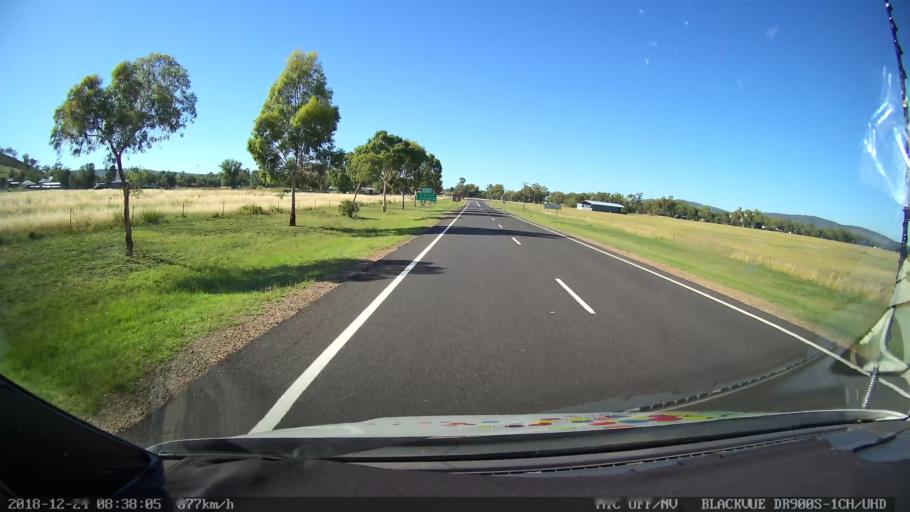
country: AU
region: New South Wales
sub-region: Liverpool Plains
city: Quirindi
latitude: -31.3376
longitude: 150.6477
